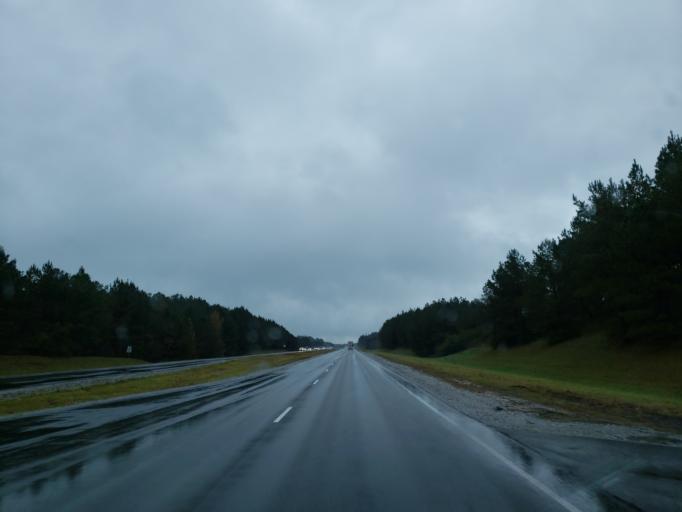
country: US
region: Mississippi
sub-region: Clarke County
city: Stonewall
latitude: 32.1857
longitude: -88.7087
